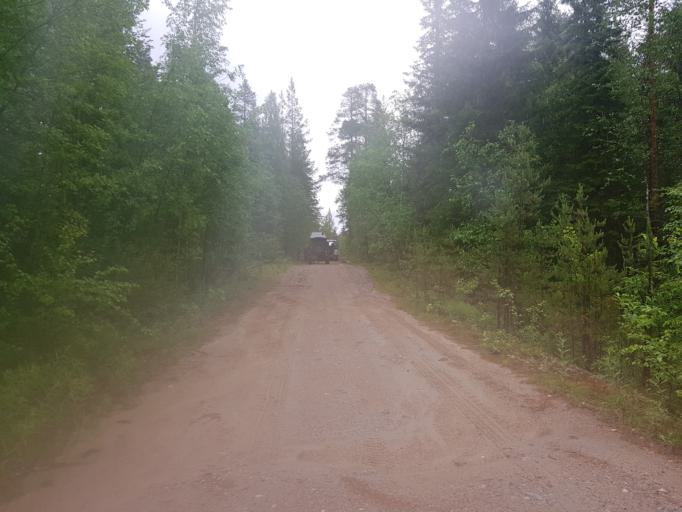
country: RU
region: Republic of Karelia
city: Kostomuksha
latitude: 64.8792
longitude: 30.2622
